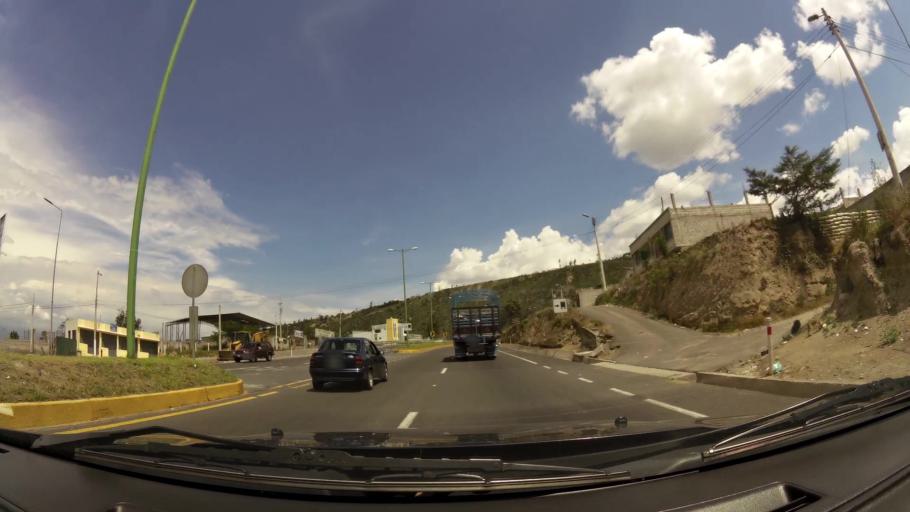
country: EC
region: Pichincha
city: Quito
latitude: -0.1019
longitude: -78.4094
